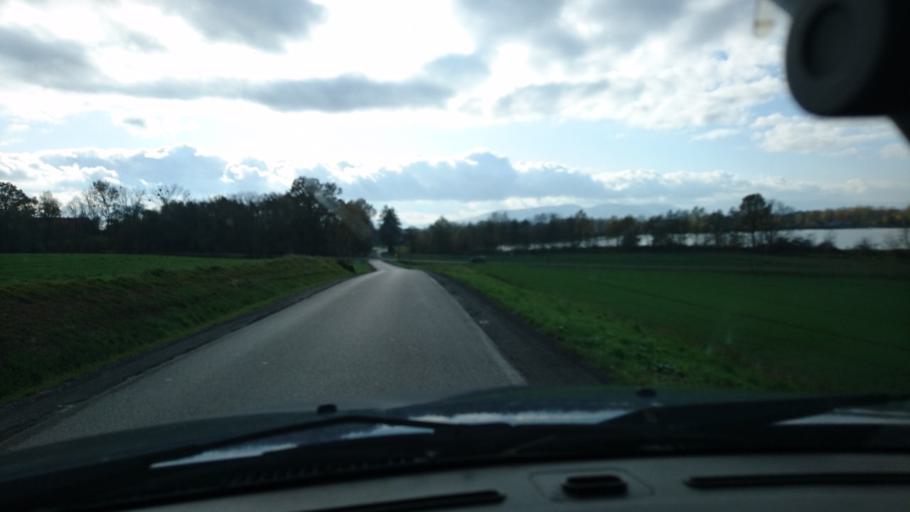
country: PL
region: Lesser Poland Voivodeship
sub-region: Powiat oswiecimski
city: Malec
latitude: 49.9407
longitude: 19.2318
